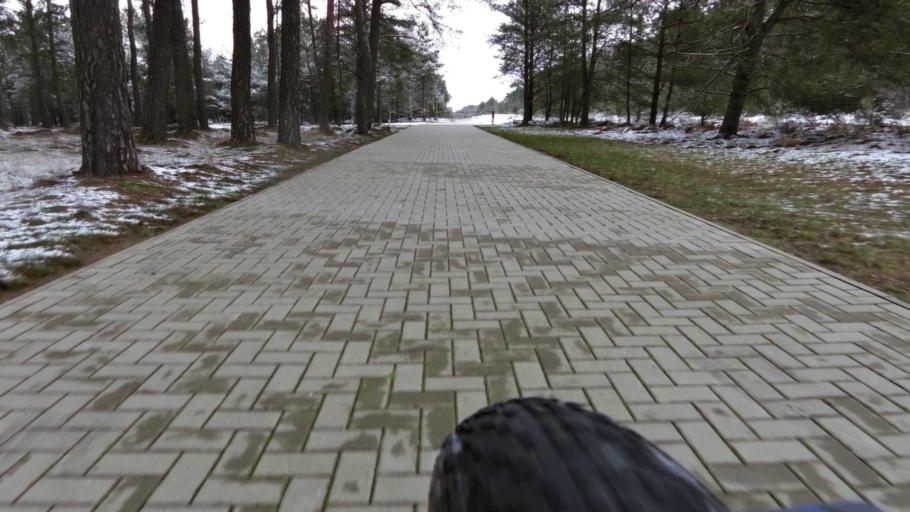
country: PL
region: West Pomeranian Voivodeship
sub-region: Powiat walecki
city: Miroslawiec
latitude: 53.3797
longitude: 16.1110
